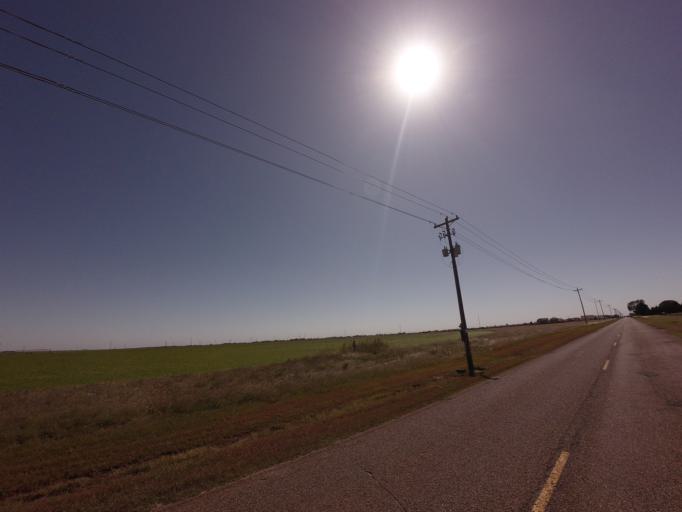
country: US
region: New Mexico
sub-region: Curry County
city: Clovis
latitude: 34.4265
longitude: -103.1603
